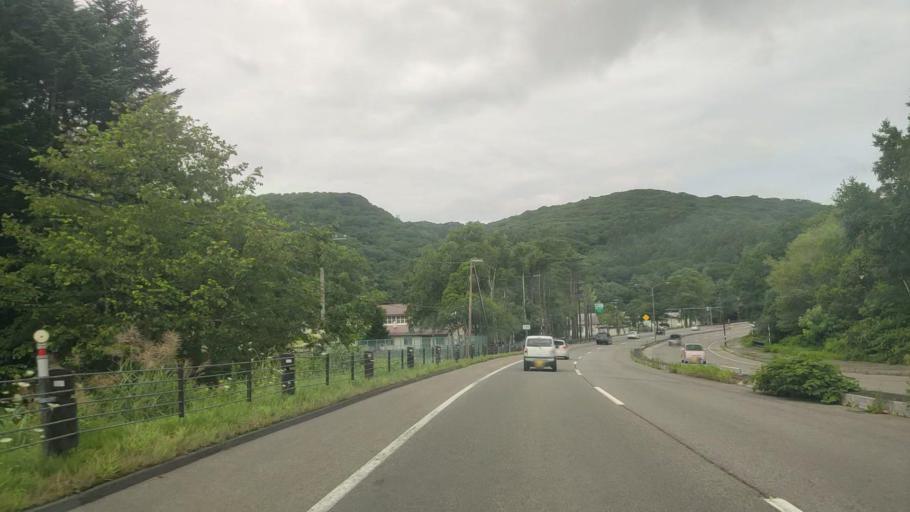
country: JP
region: Hokkaido
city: Nanae
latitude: 41.9595
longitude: 140.6482
